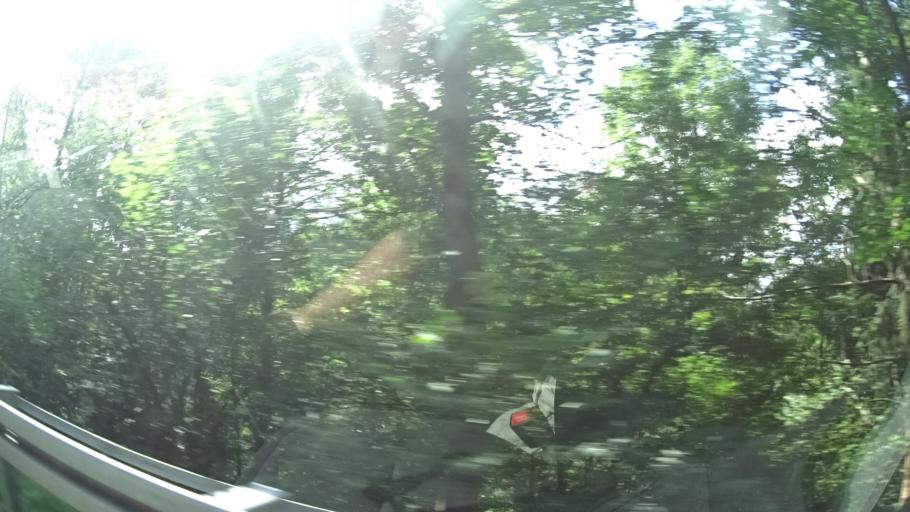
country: DE
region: Thuringia
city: Grafenthal
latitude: 50.5092
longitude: 11.2978
